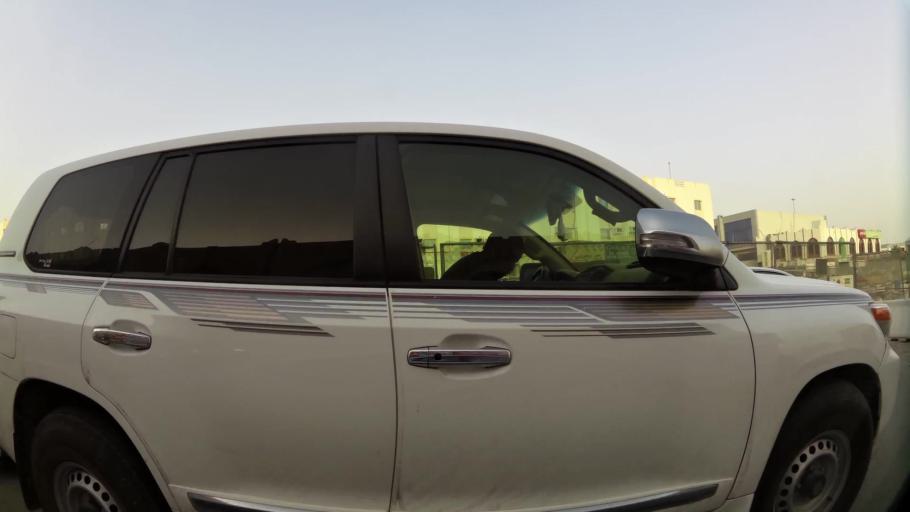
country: QA
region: Baladiyat ar Rayyan
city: Ar Rayyan
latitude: 25.2414
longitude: 51.4556
